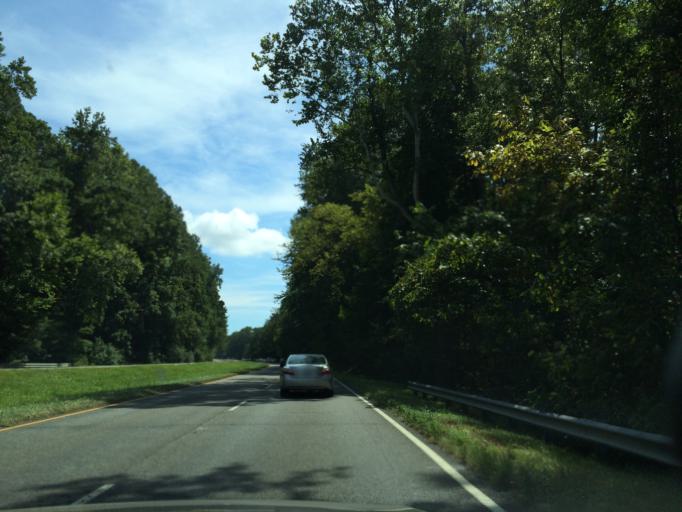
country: US
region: Virginia
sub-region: York County
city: Yorktown
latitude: 37.2082
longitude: -76.5105
